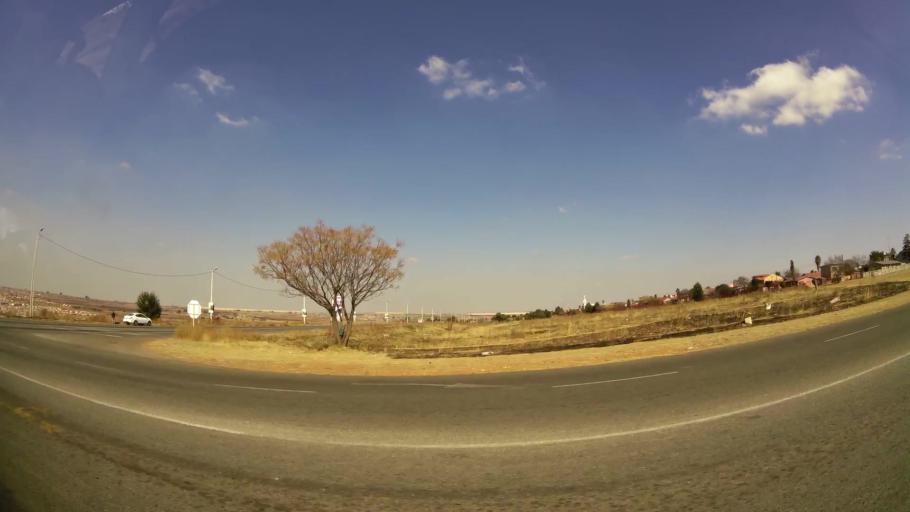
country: ZA
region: Gauteng
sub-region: West Rand District Municipality
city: Randfontein
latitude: -26.1643
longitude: 27.7610
